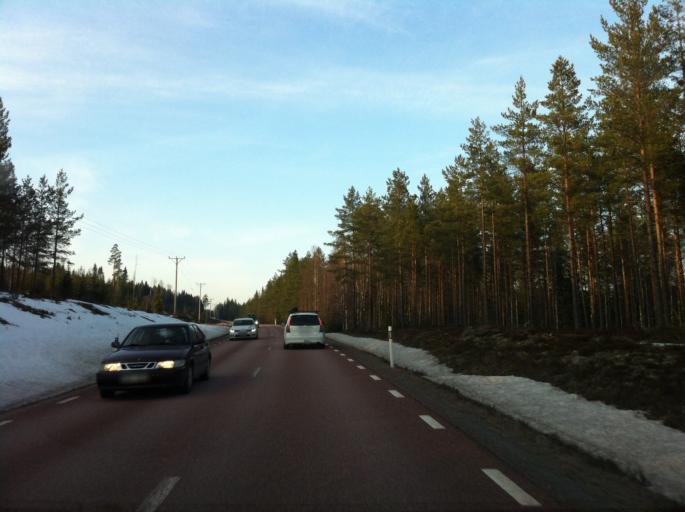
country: SE
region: Vaermland
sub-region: Filipstads Kommun
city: Lesjofors
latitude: 60.1863
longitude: 14.1967
